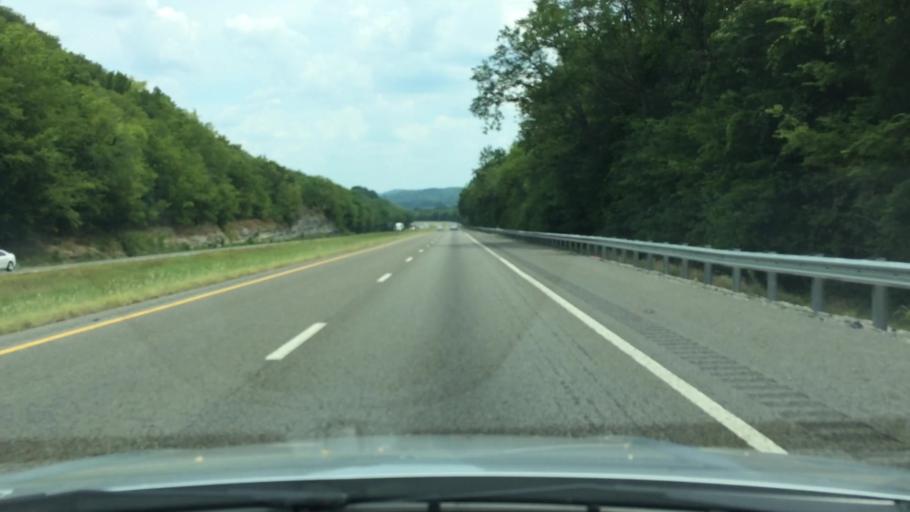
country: US
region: Tennessee
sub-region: Marshall County
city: Cornersville
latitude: 35.4060
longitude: -86.8802
